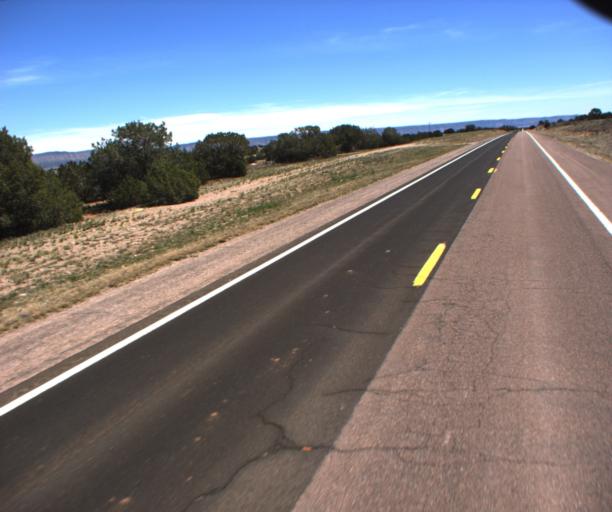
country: US
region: Arizona
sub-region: Mohave County
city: Peach Springs
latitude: 35.5172
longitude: -113.1997
